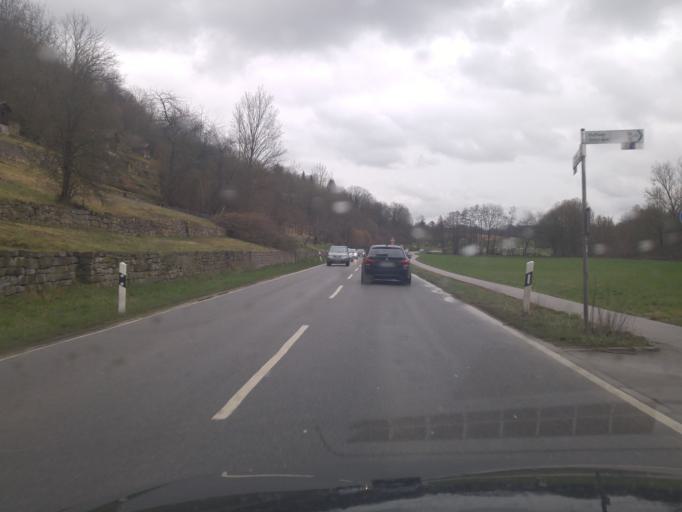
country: DE
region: Baden-Wuerttemberg
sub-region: Regierungsbezirk Stuttgart
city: Steinheim am der Murr
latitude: 48.9607
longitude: 9.2899
